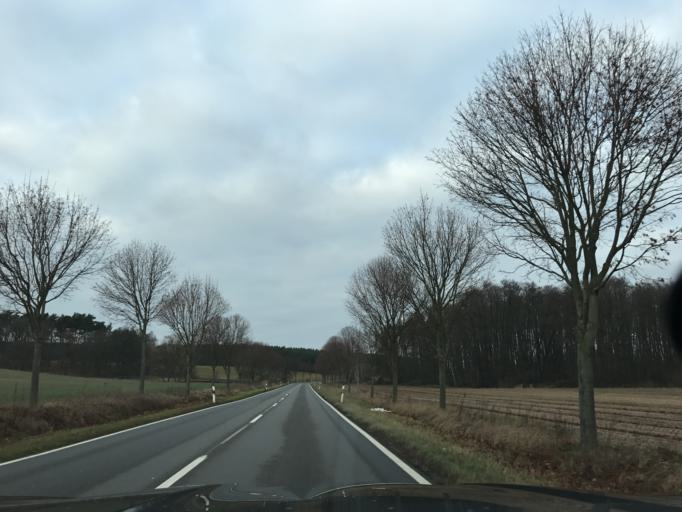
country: DE
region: Brandenburg
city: Golzow
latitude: 52.3521
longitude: 12.6144
